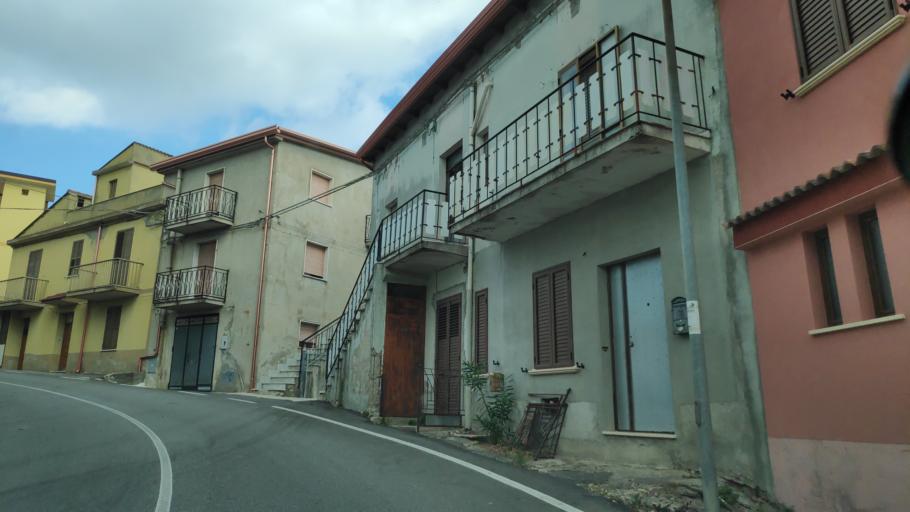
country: IT
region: Calabria
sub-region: Provincia di Catanzaro
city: Santa Caterina dello Ionio
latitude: 38.5319
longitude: 16.5223
